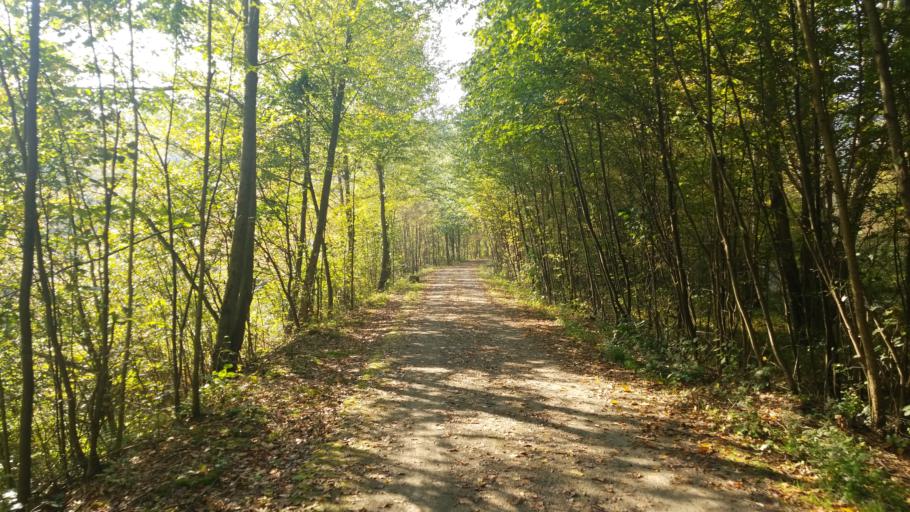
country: US
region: Pennsylvania
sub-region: Jefferson County
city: Brockway
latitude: 41.3553
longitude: -78.8180
